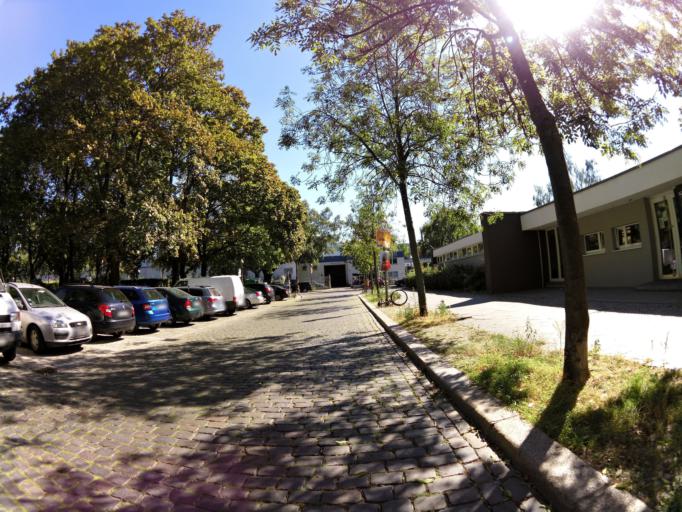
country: DE
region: Berlin
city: Wedding Bezirk
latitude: 52.5411
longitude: 13.3606
